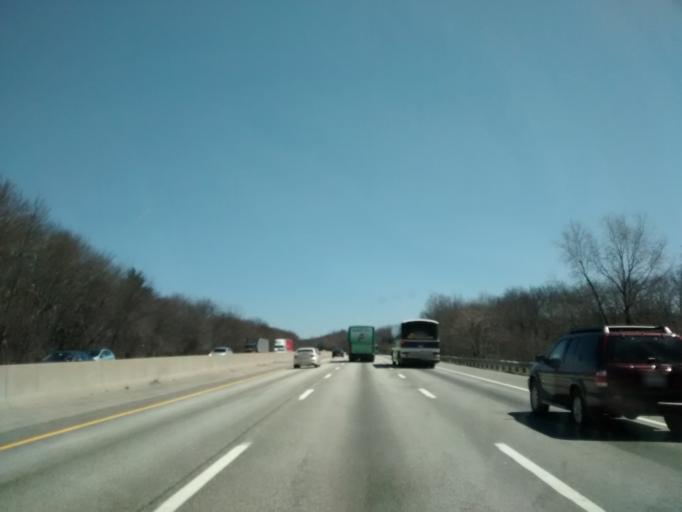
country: US
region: Massachusetts
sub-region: Worcester County
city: Westborough
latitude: 42.2271
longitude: -71.6395
